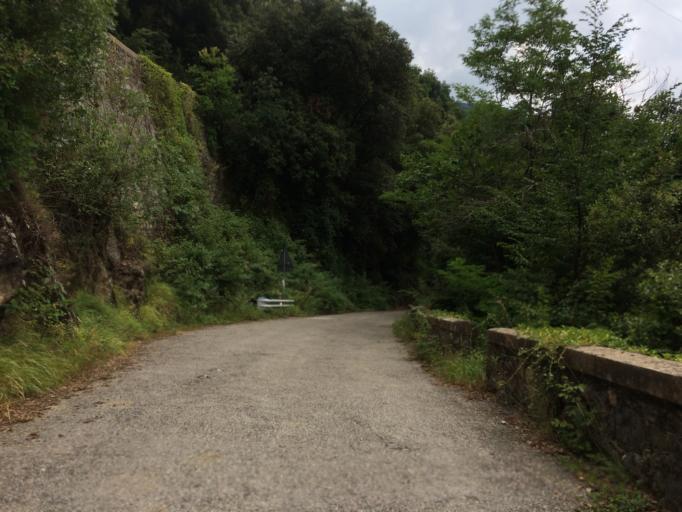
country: IT
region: Liguria
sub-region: Provincia di Imperia
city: Castel Vittorio
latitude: 43.9429
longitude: 7.6858
